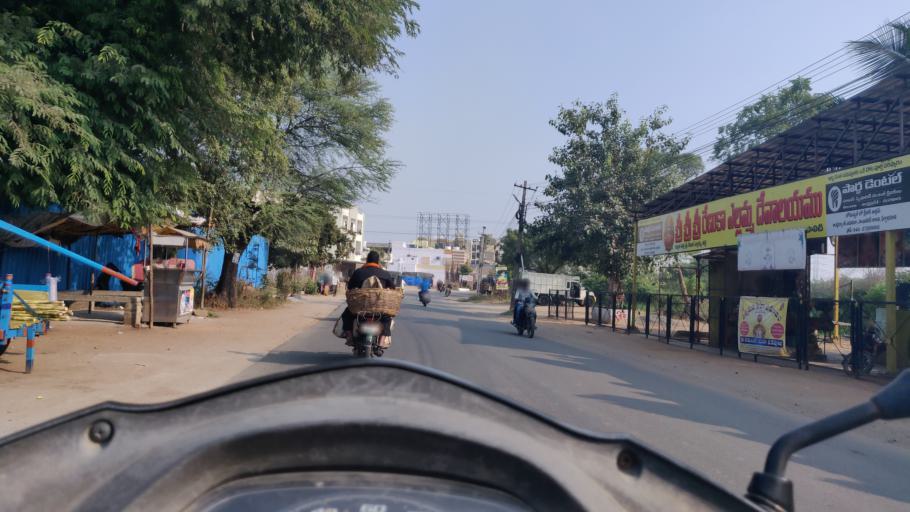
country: IN
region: Telangana
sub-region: Rangareddi
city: Uppal Kalan
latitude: 17.3999
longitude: 78.5838
